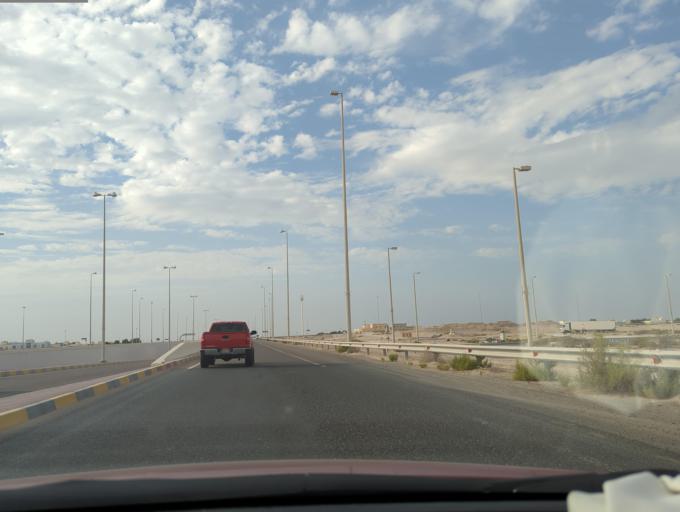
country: AE
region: Abu Dhabi
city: Abu Dhabi
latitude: 24.3979
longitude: 54.7556
